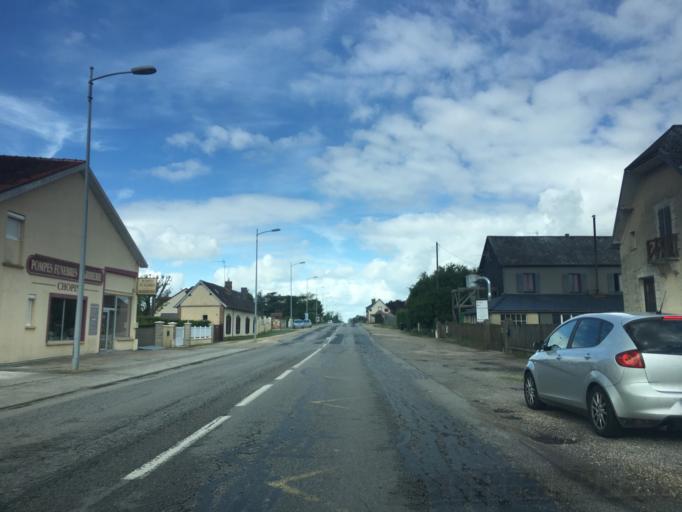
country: FR
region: Haute-Normandie
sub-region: Departement de l'Eure
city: Verneuil-sur-Avre
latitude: 48.7383
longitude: 0.9174
